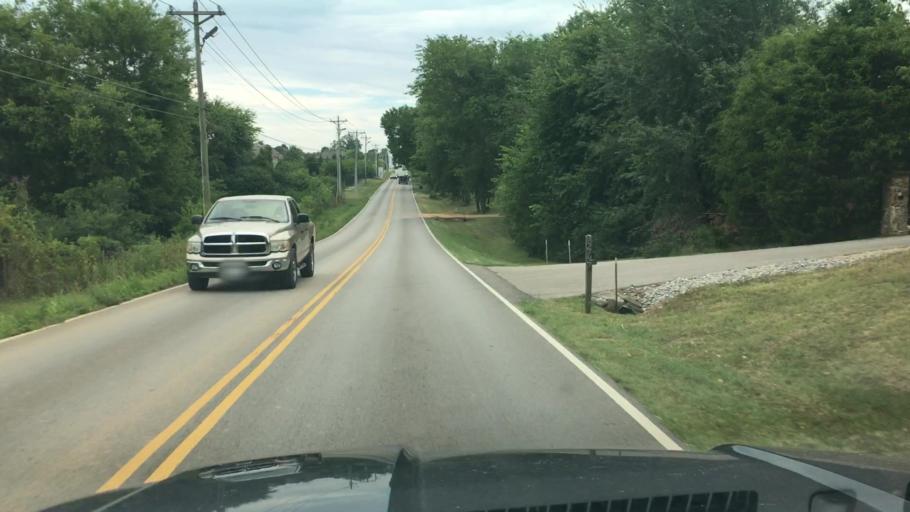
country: US
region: Tennessee
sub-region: Williamson County
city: Thompson's Station
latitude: 35.7644
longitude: -86.8818
